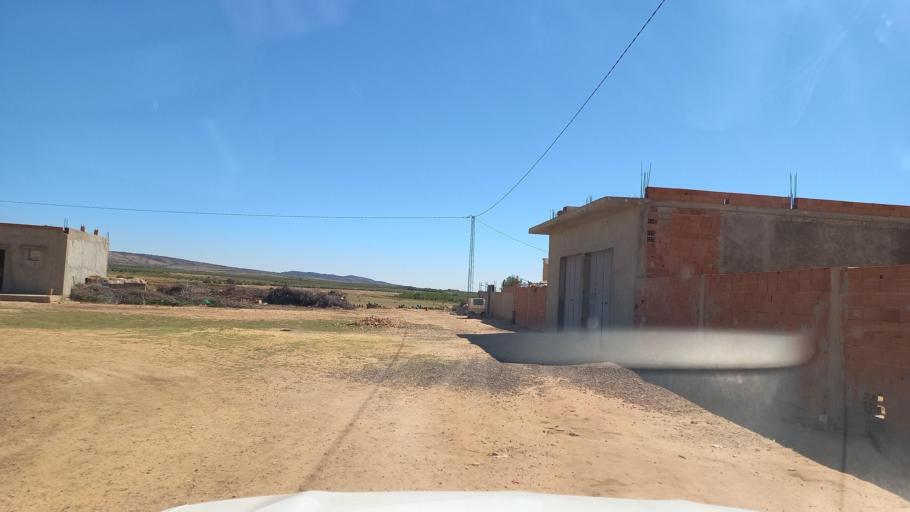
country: TN
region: Al Qasrayn
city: Sbiba
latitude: 35.3590
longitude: 9.0866
